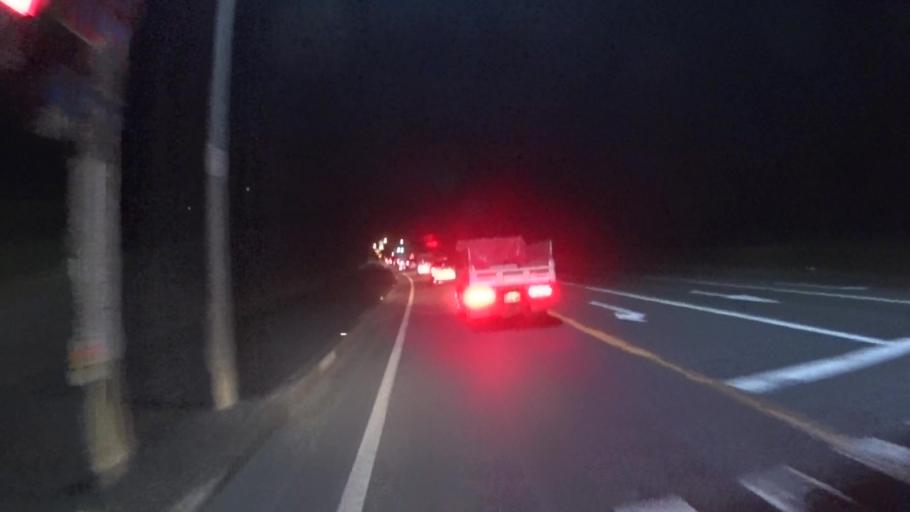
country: JP
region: Kyoto
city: Ayabe
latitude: 35.2604
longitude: 135.4087
